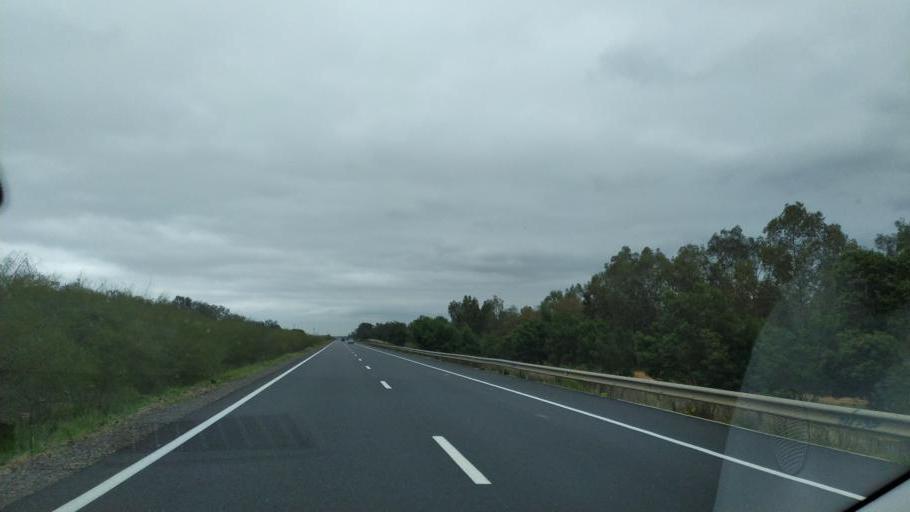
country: MA
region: Gharb-Chrarda-Beni Hssen
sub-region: Kenitra Province
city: Kenitra
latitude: 34.1786
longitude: -6.6535
